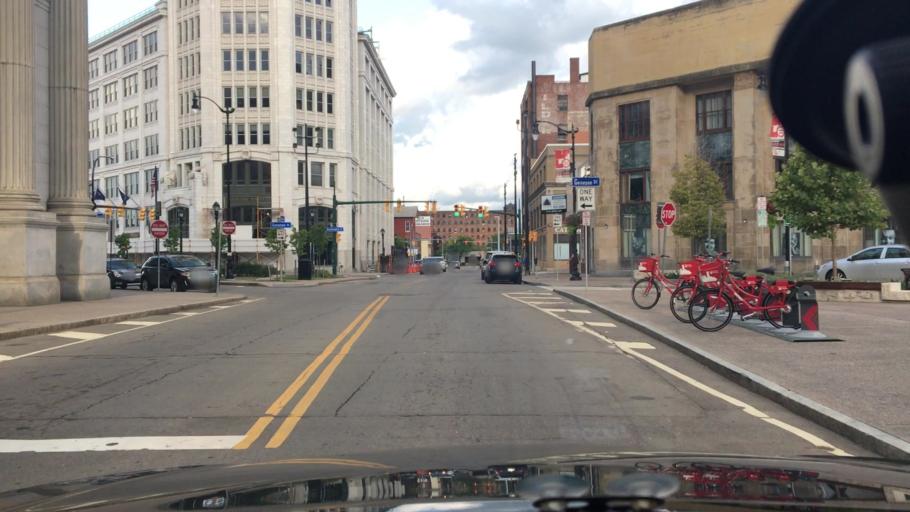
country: US
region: New York
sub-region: Erie County
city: Buffalo
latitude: 42.8886
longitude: -78.8733
